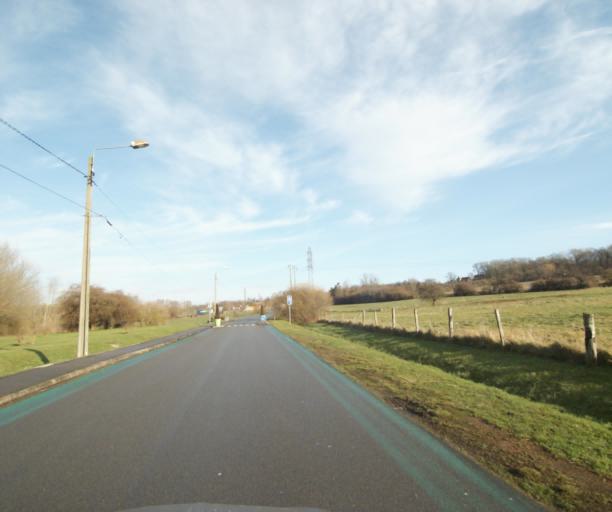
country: FR
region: Nord-Pas-de-Calais
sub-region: Departement du Nord
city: Trith-Saint-Leger
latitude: 50.3189
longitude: 3.4961
